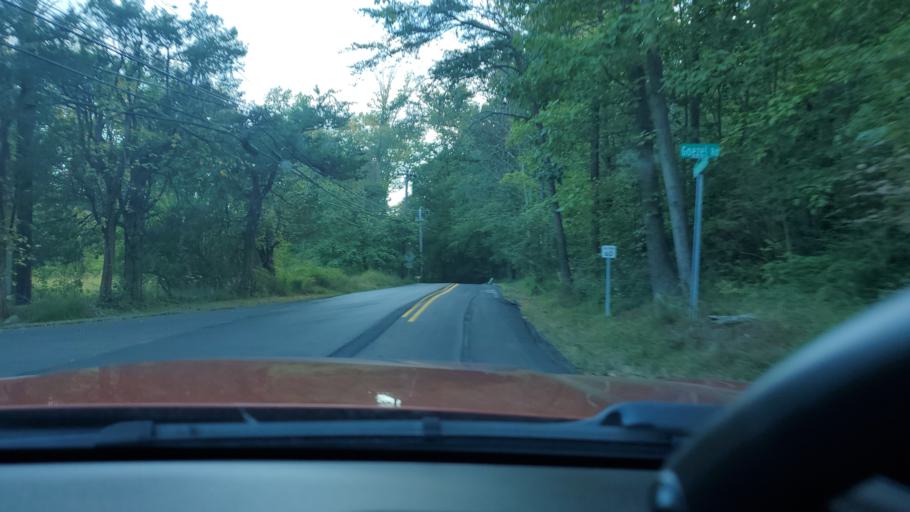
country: US
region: Pennsylvania
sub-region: Montgomery County
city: Woxall
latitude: 40.3181
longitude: -75.4899
